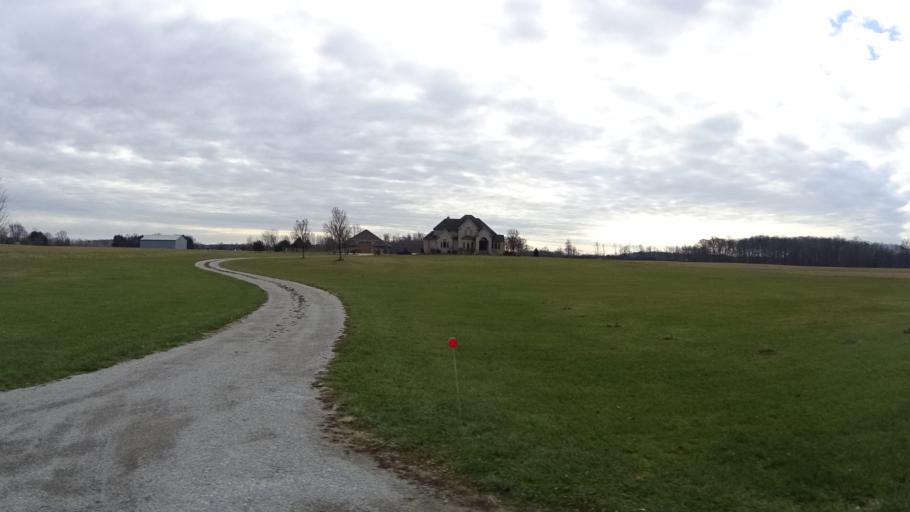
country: US
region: Ohio
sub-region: Lorain County
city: Camden
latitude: 41.2760
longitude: -82.3215
